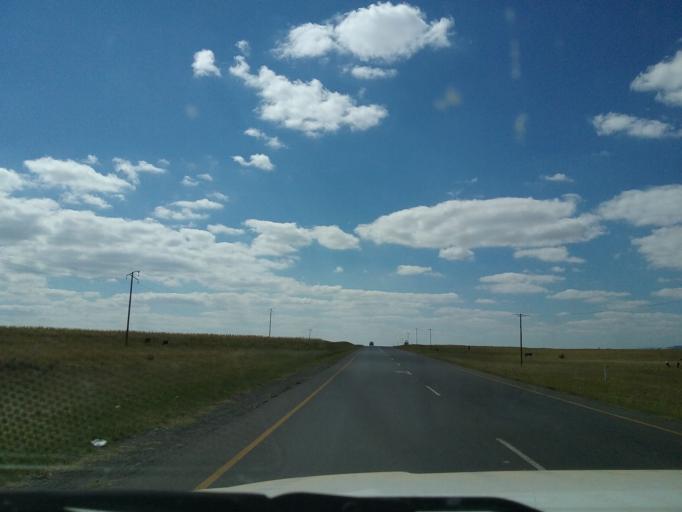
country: LS
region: Maseru
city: Maseru
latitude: -29.4769
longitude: 27.5298
